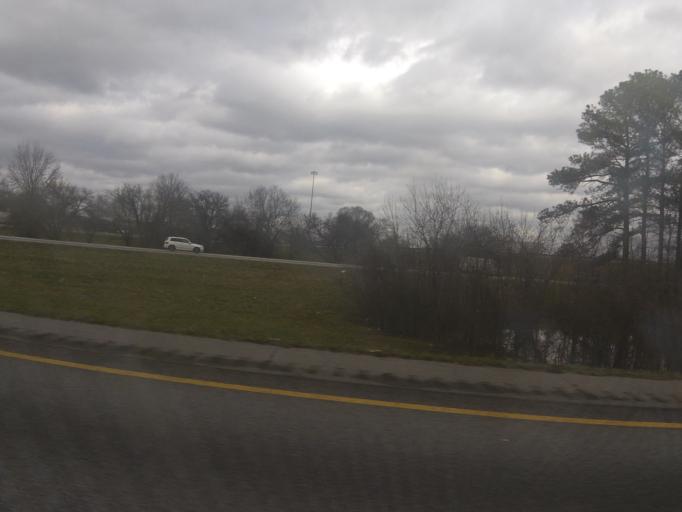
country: US
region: Tennessee
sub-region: Hamilton County
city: East Ridge
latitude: 35.0036
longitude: -85.2155
